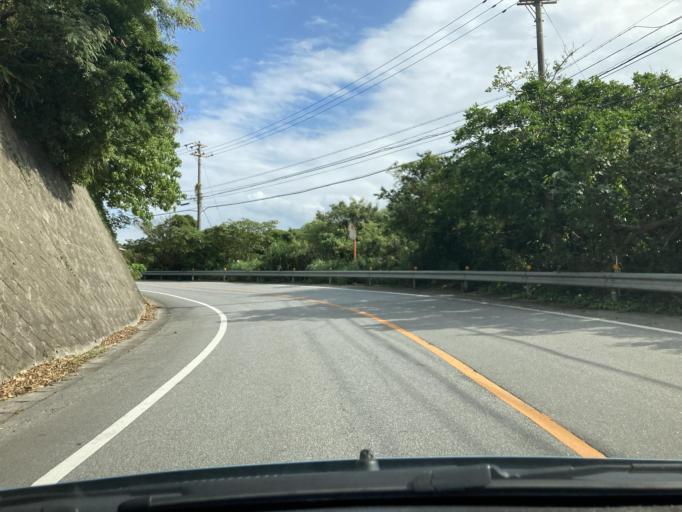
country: JP
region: Okinawa
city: Ginowan
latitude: 26.2693
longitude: 127.7826
